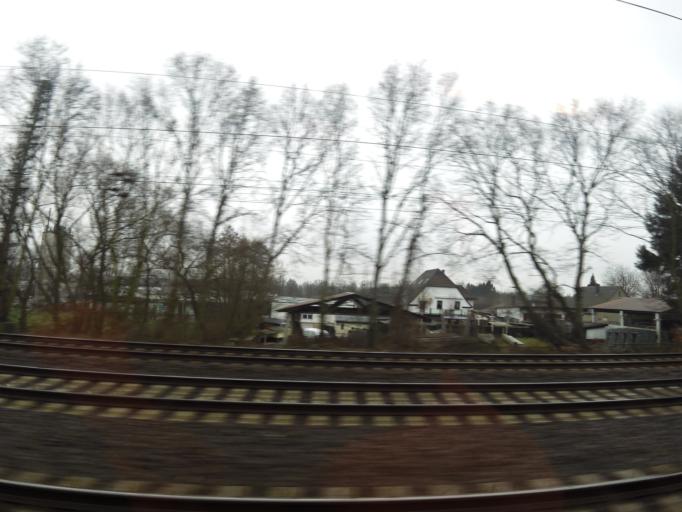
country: DE
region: North Rhine-Westphalia
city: Loehne
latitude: 52.1986
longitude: 8.7432
